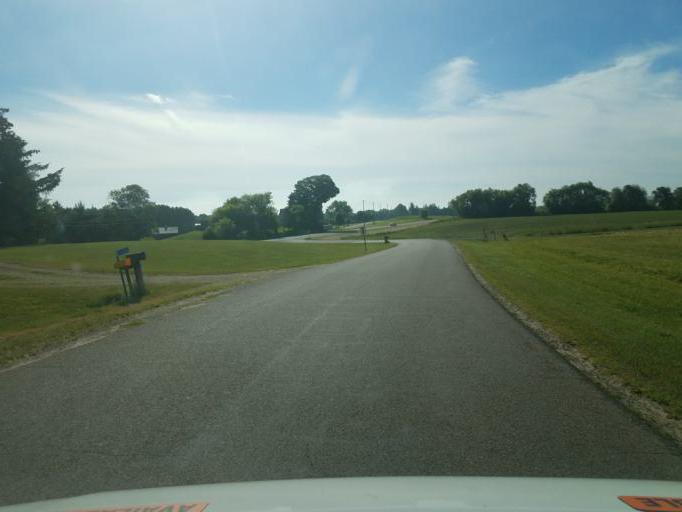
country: US
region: Wisconsin
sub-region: Sauk County
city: Reedsburg
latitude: 43.5395
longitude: -90.0350
